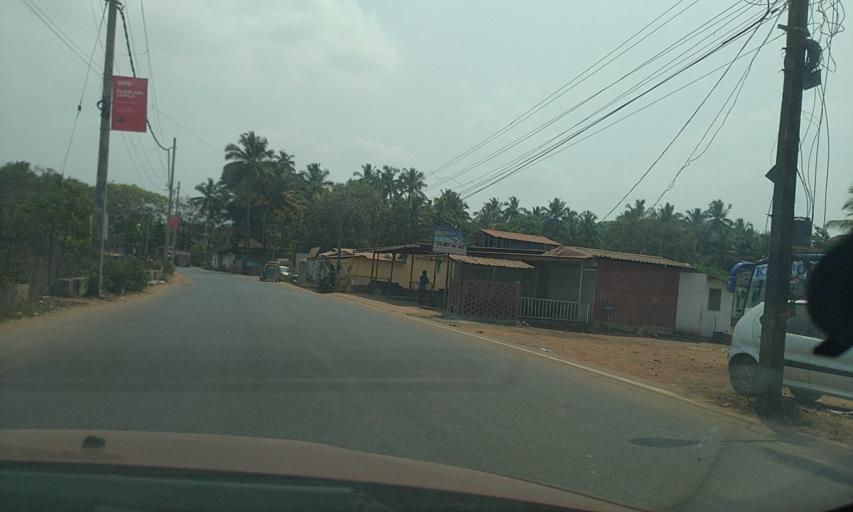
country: IN
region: Goa
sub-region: North Goa
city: Vagator
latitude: 15.5900
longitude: 73.7656
